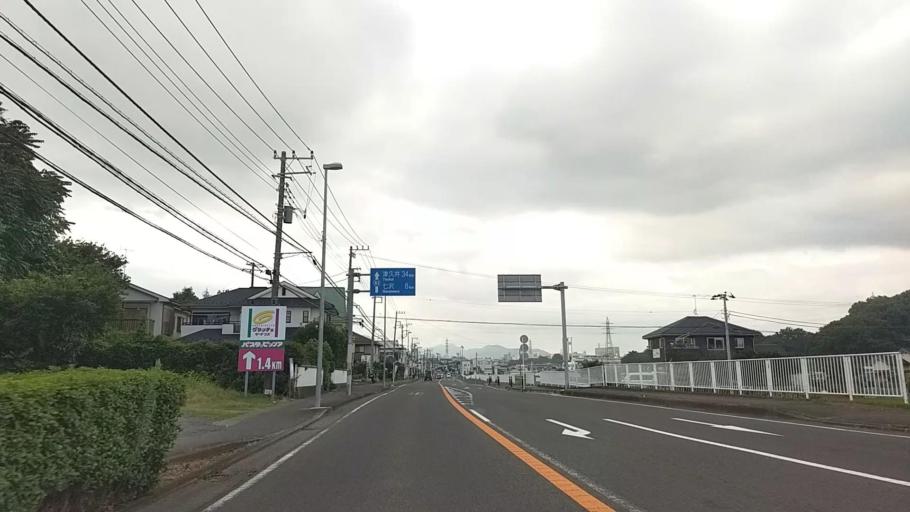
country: JP
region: Kanagawa
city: Isehara
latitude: 35.3793
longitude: 139.3178
